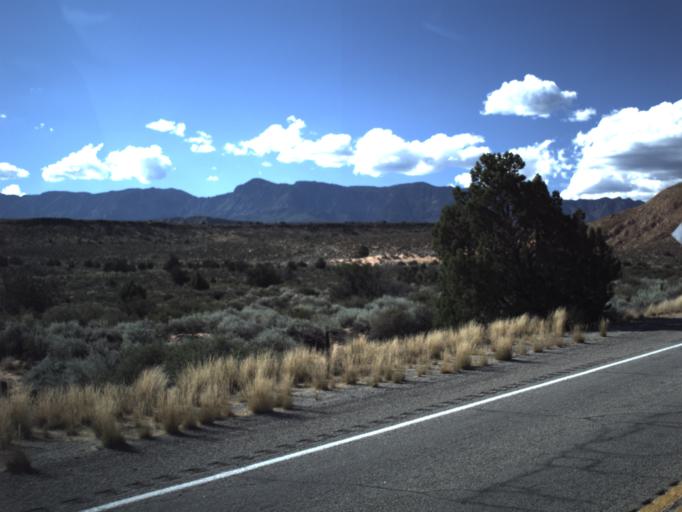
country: US
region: Utah
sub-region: Washington County
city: Toquerville
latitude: 37.2628
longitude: -113.2949
